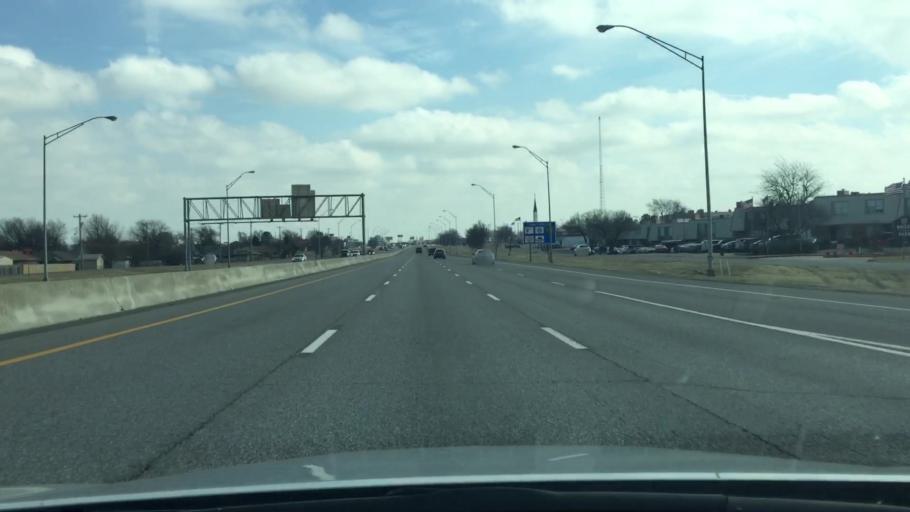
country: US
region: Oklahoma
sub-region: Oklahoma County
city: Oklahoma City
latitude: 35.3932
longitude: -97.5619
